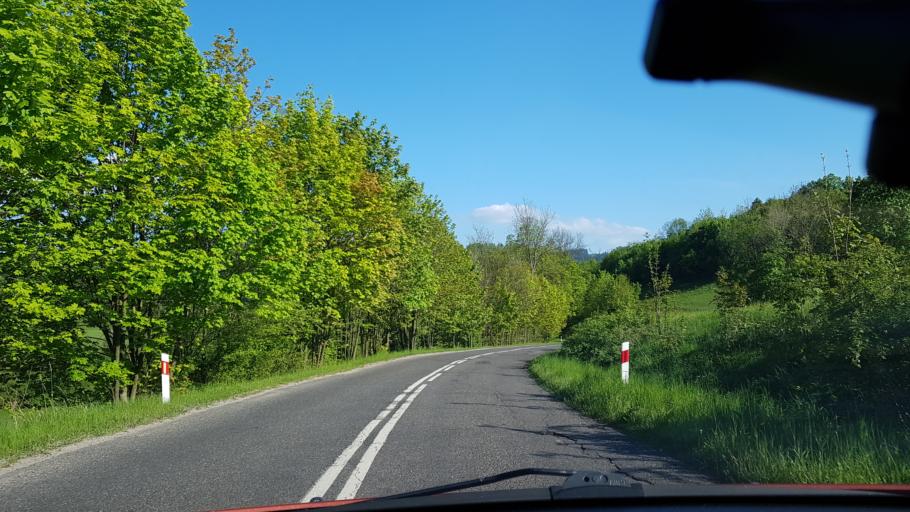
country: PL
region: Lower Silesian Voivodeship
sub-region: Powiat klodzki
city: Bozkow
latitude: 50.5728
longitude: 16.6079
